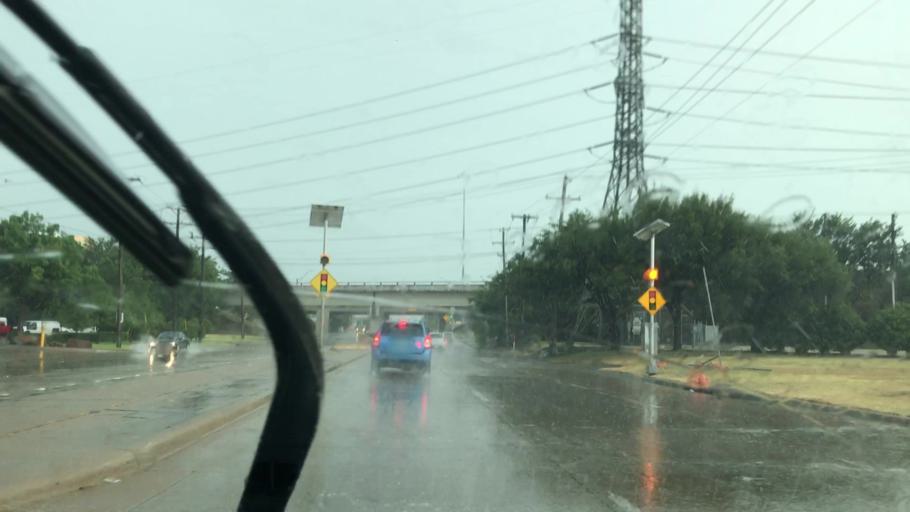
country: US
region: Texas
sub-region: Dallas County
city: Garland
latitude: 32.8877
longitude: -96.7004
